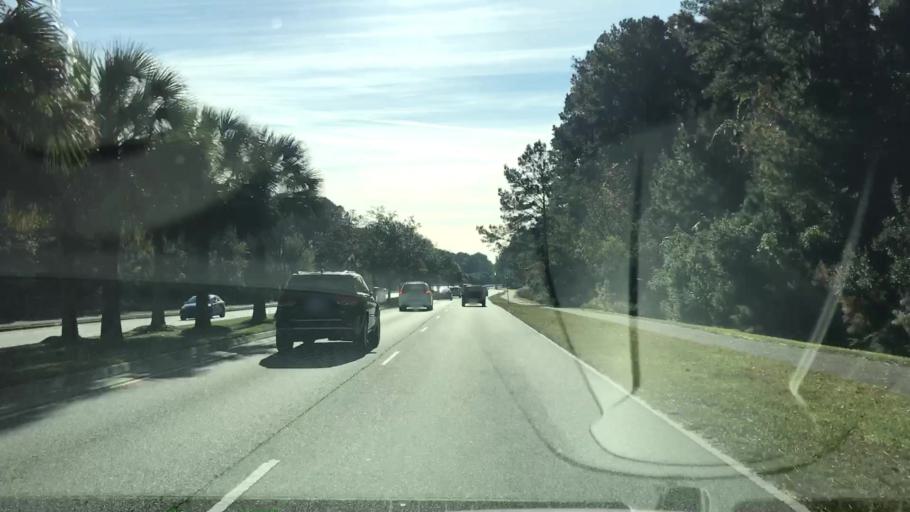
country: US
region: South Carolina
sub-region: Beaufort County
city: Bluffton
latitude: 32.2598
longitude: -80.9049
